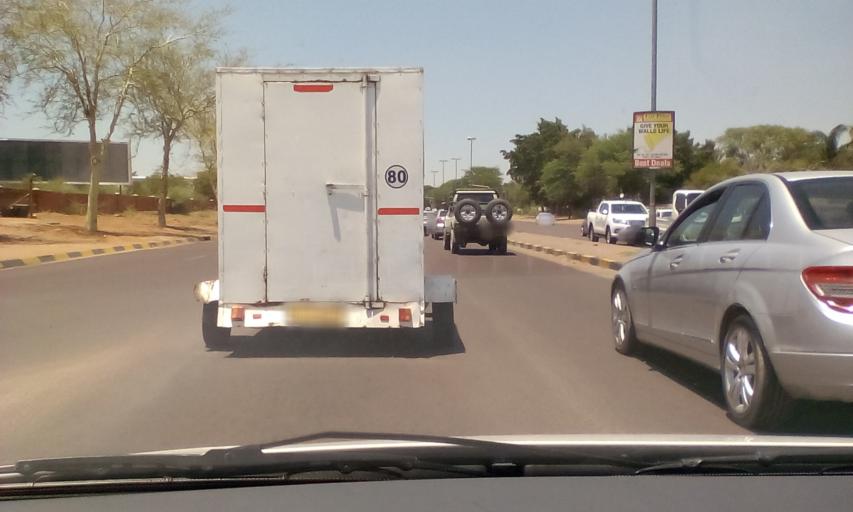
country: BW
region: South East
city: Gaborone
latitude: -24.6558
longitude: 25.9003
